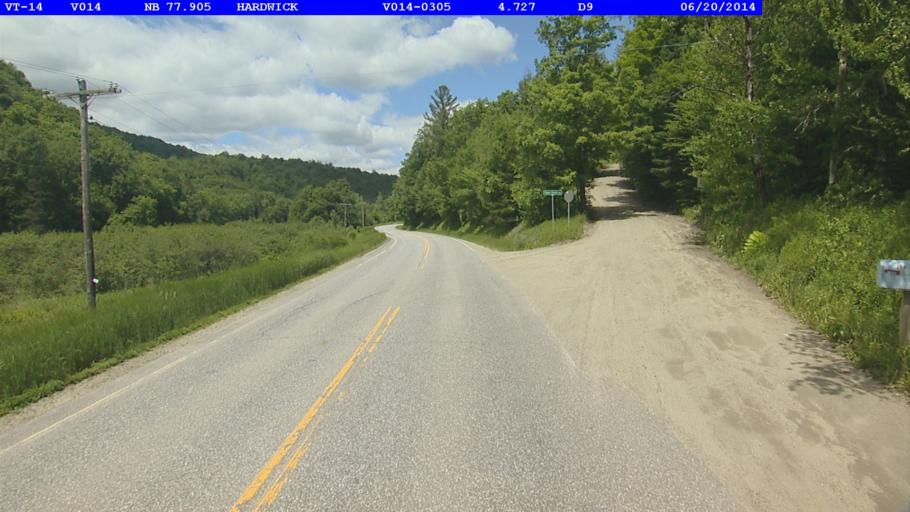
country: US
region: Vermont
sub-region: Caledonia County
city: Hardwick
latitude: 44.5616
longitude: -72.3677
